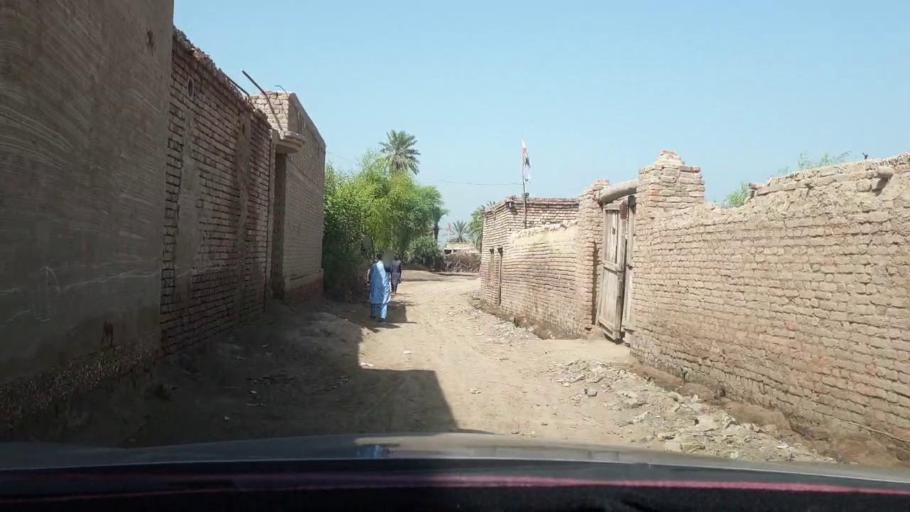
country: PK
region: Sindh
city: Kambar
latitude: 27.5990
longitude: 67.9742
